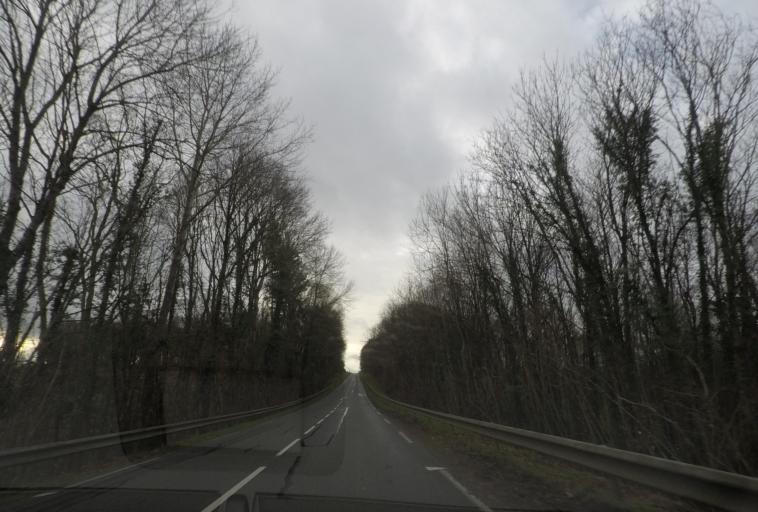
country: FR
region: Pays de la Loire
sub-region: Departement de la Sarthe
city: Saint-Calais
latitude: 47.9668
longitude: 0.7577
